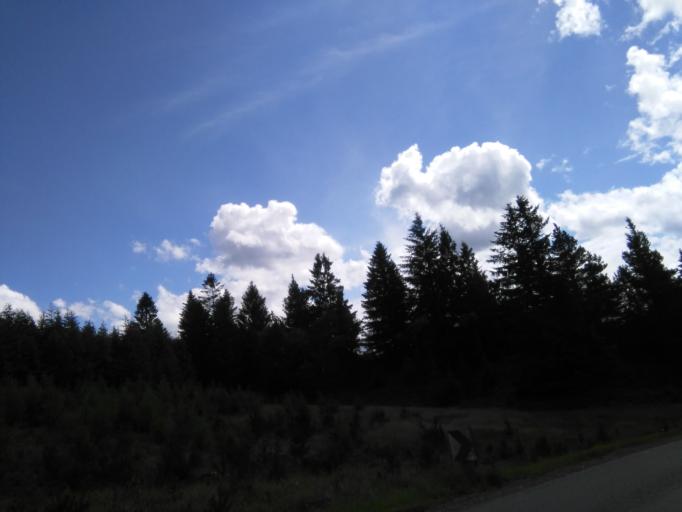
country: DK
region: Central Jutland
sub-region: Silkeborg Kommune
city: Virklund
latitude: 56.0860
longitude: 9.4287
